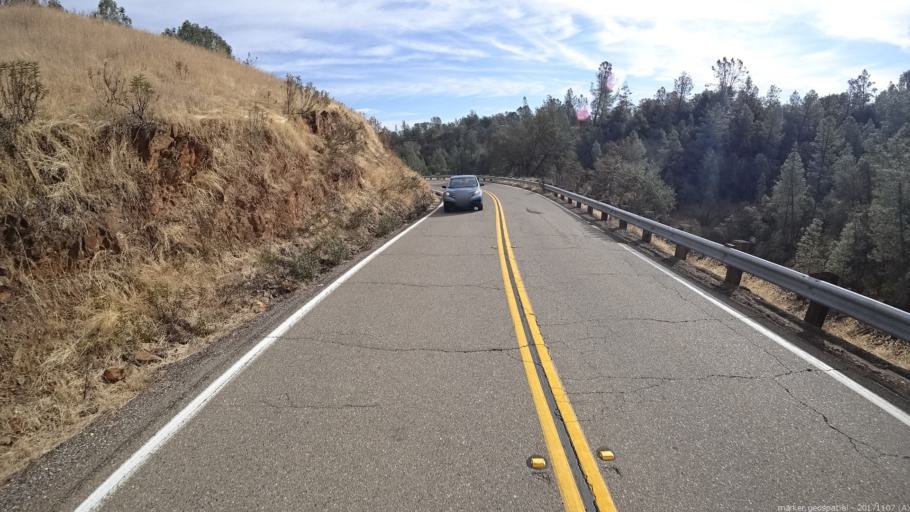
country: US
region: California
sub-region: Shasta County
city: Shasta
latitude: 40.5098
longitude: -122.5251
